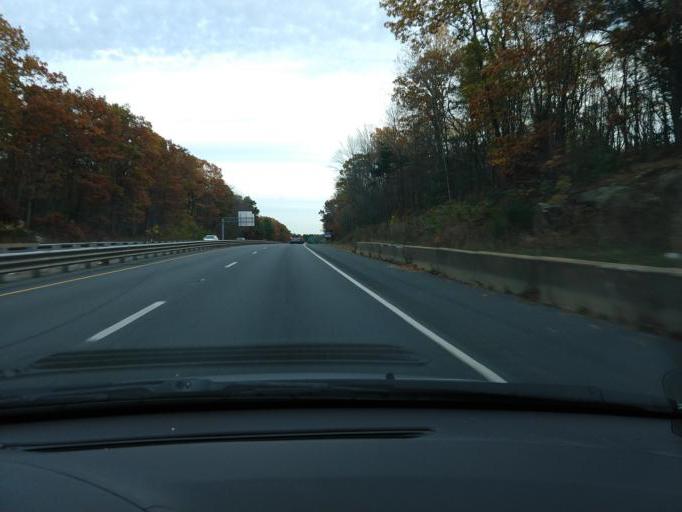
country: US
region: Massachusetts
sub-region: Middlesex County
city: Littleton Common
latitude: 42.5142
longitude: -71.4950
